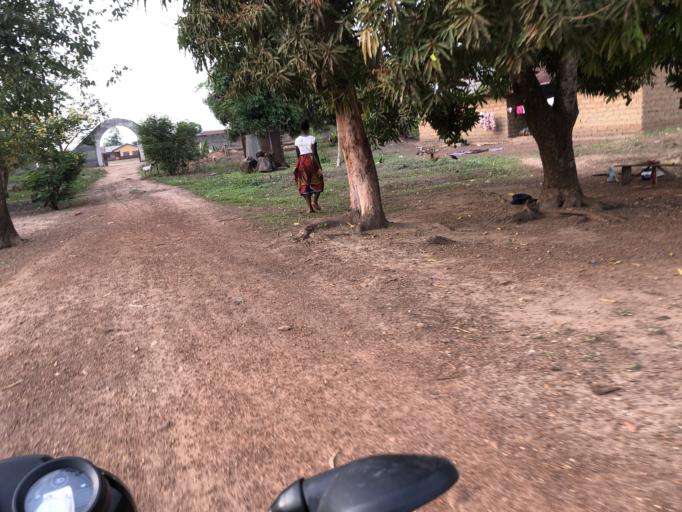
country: SL
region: Northern Province
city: Yonibana
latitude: 8.4686
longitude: -12.2036
